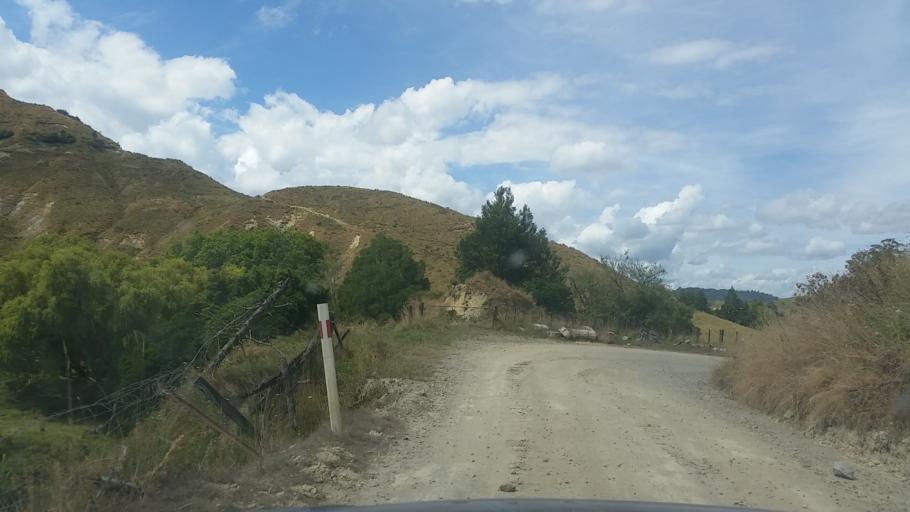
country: NZ
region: Taranaki
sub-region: New Plymouth District
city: Waitara
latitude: -39.0969
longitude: 174.8387
